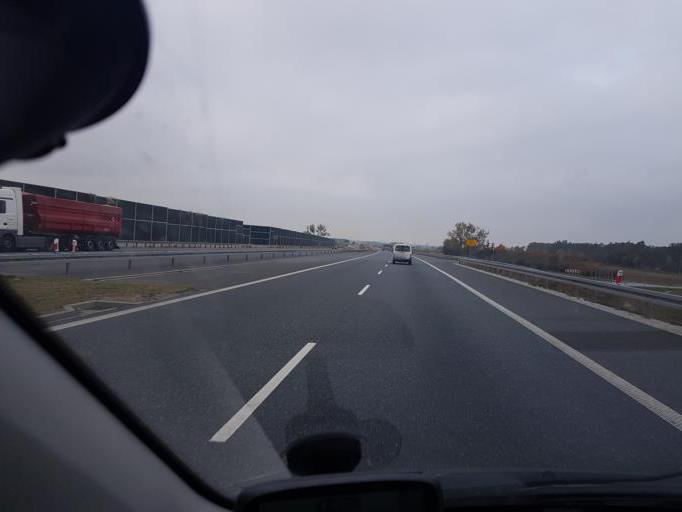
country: PL
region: Kujawsko-Pomorskie
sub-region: Powiat wloclawski
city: Brzesc Kujawski
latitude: 52.6285
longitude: 18.9603
